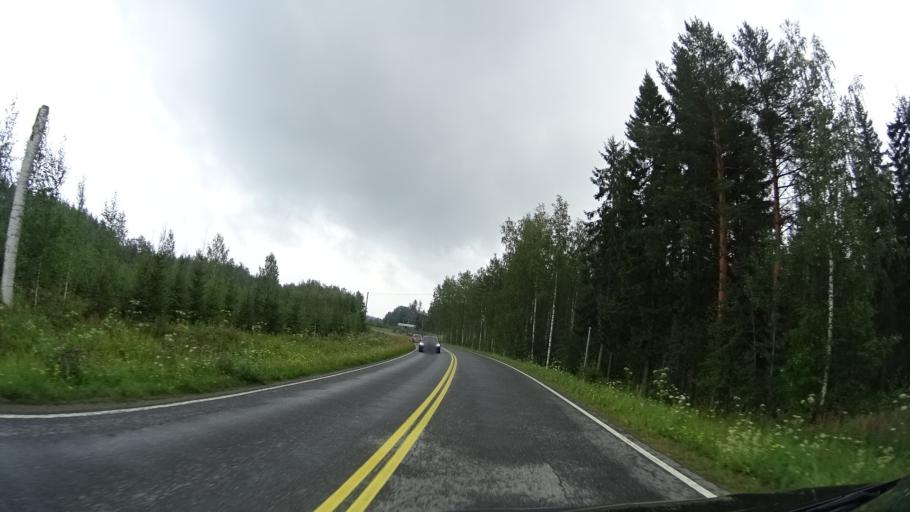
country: FI
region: North Karelia
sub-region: Keski-Karjala
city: Raeaekkylae
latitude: 62.3055
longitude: 29.5424
